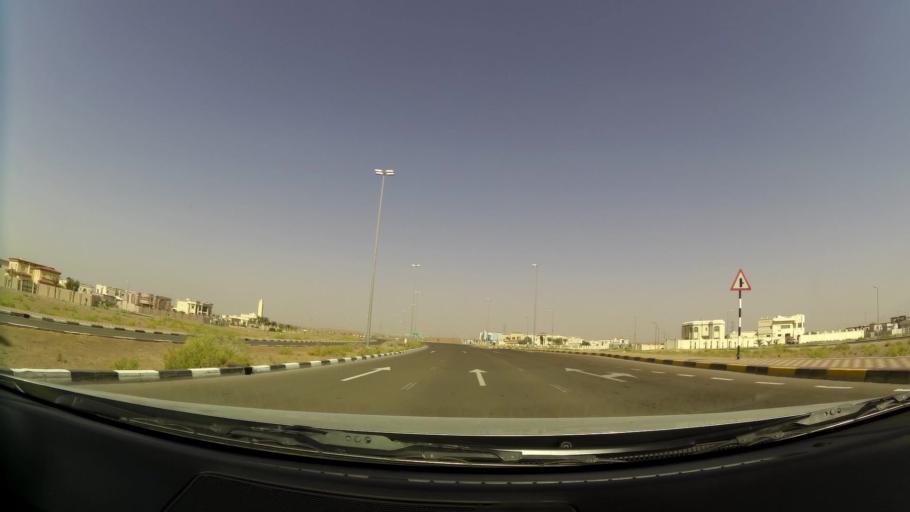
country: OM
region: Al Buraimi
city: Al Buraymi
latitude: 24.3443
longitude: 55.7847
